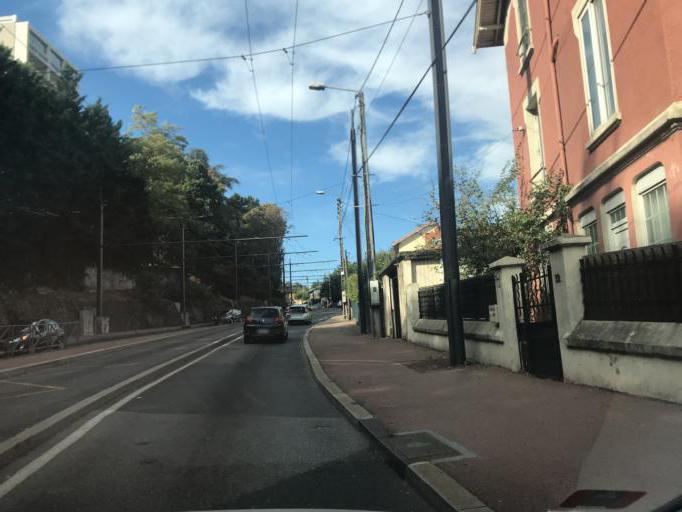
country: FR
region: Rhone-Alpes
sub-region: Departement du Rhone
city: Caluire-et-Cuire
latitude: 45.7955
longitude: 4.8586
